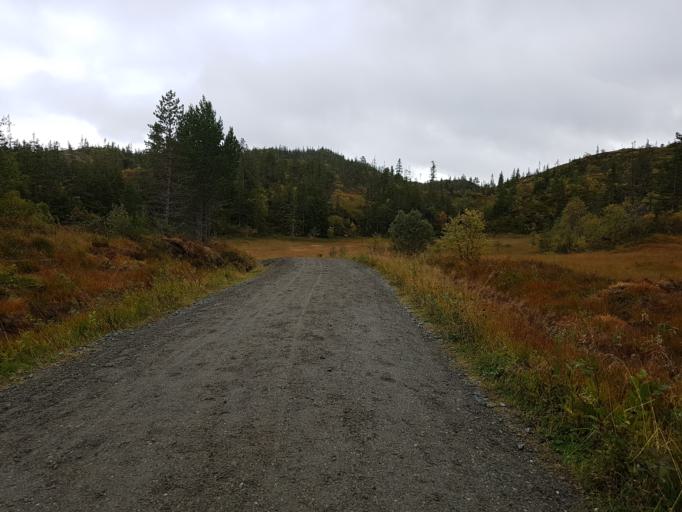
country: NO
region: Sor-Trondelag
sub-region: Melhus
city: Melhus
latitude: 63.4189
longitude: 10.2163
